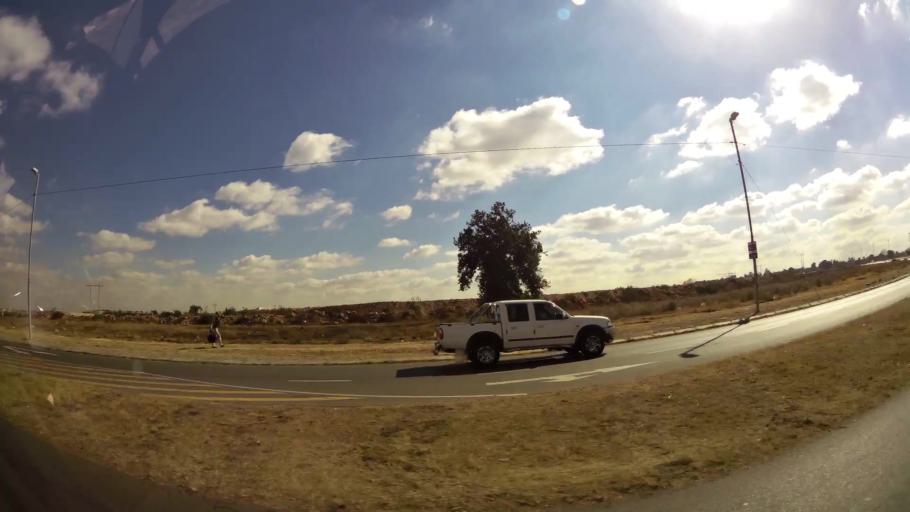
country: ZA
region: Gauteng
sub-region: West Rand District Municipality
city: Krugersdorp
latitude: -26.1372
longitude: 27.7991
